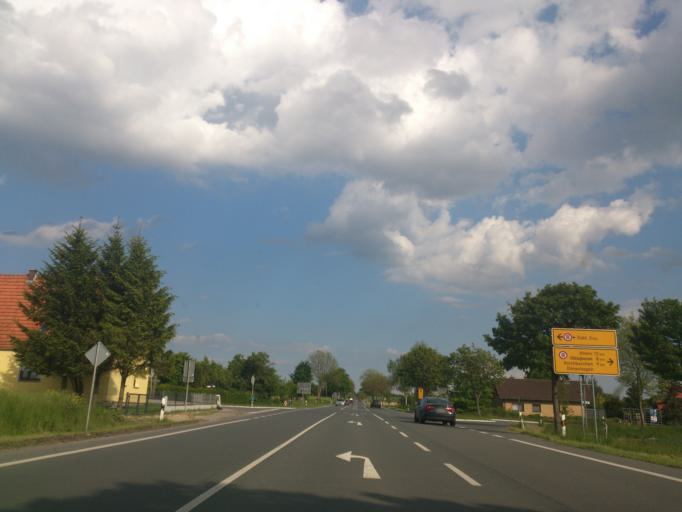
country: DE
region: North Rhine-Westphalia
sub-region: Regierungsbezirk Detmold
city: Paderborn
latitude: 51.6777
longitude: 8.8309
